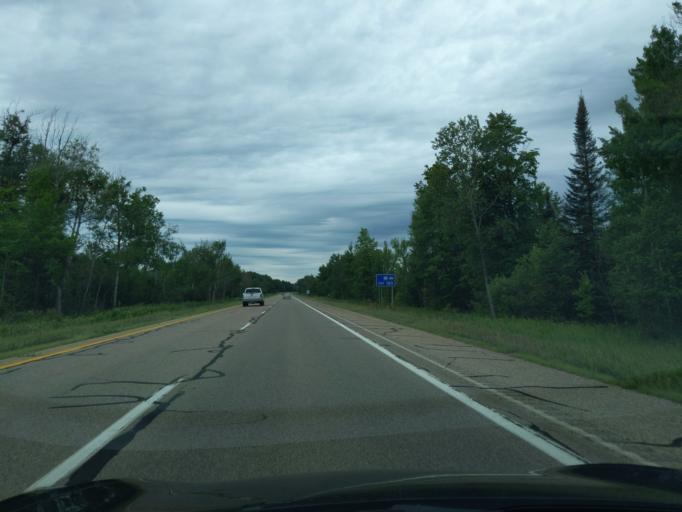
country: US
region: Michigan
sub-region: Roscommon County
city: Houghton Lake
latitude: 44.2849
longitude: -84.8007
